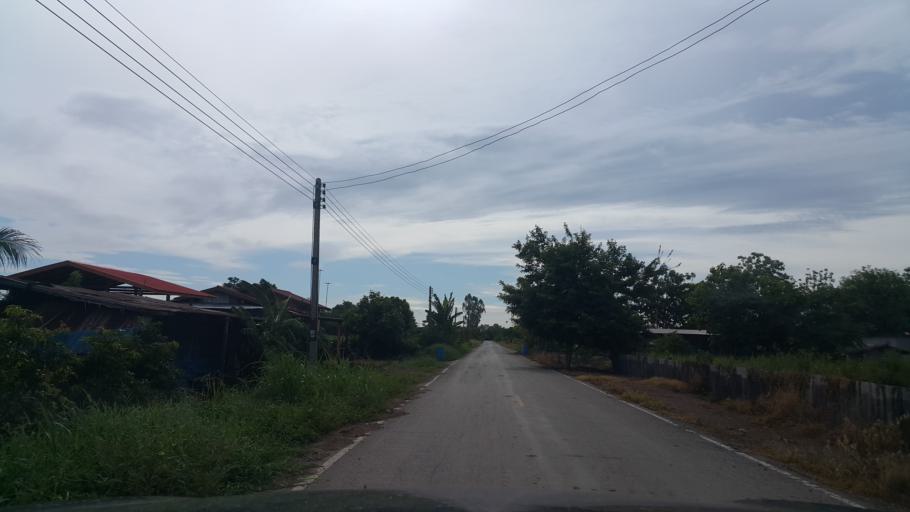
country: TH
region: Sukhothai
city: Sawankhalok
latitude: 17.2678
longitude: 99.9226
